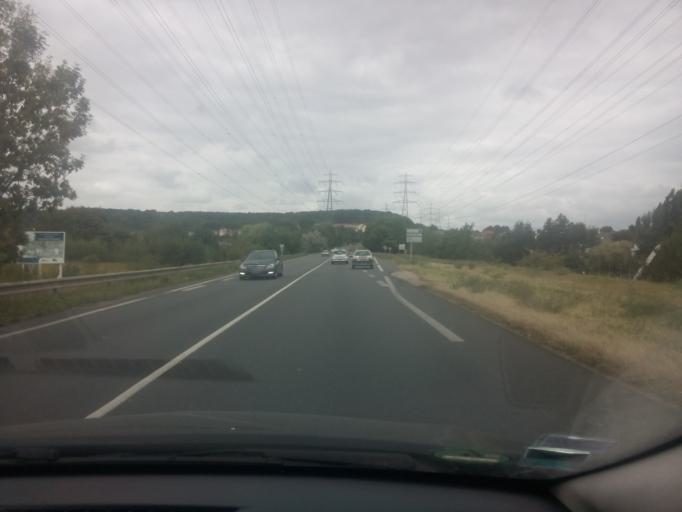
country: FR
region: Ile-de-France
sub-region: Departement de l'Essonne
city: Igny
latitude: 48.7342
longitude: 2.2317
